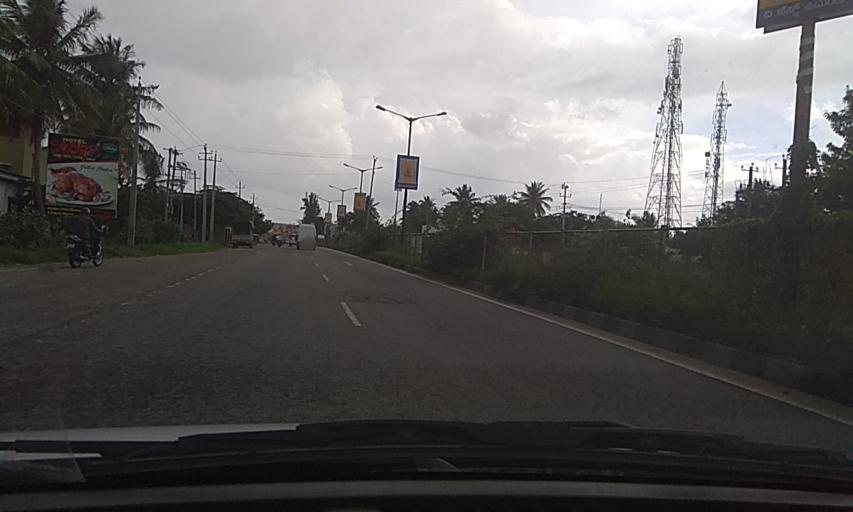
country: IN
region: Karnataka
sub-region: Mandya
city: Shrirangapattana
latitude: 12.3636
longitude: 76.6624
